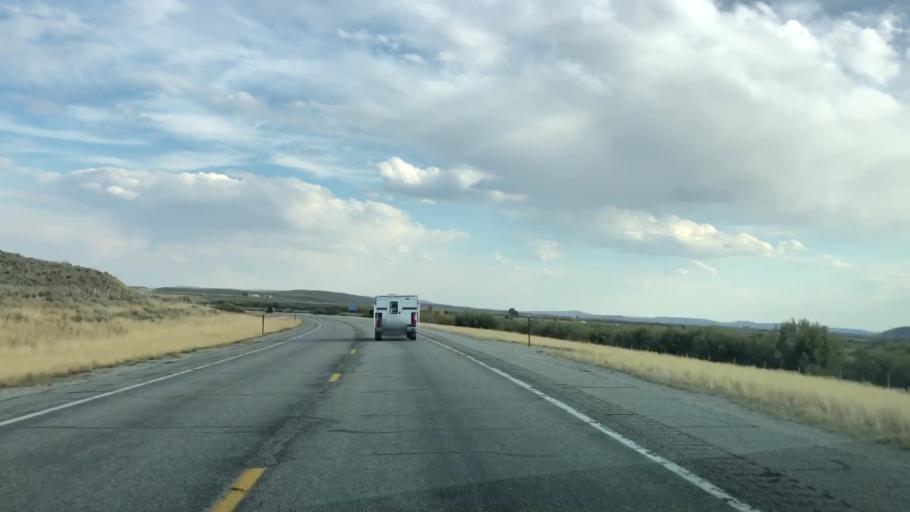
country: US
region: Wyoming
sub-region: Sublette County
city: Pinedale
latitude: 43.0228
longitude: -110.1230
